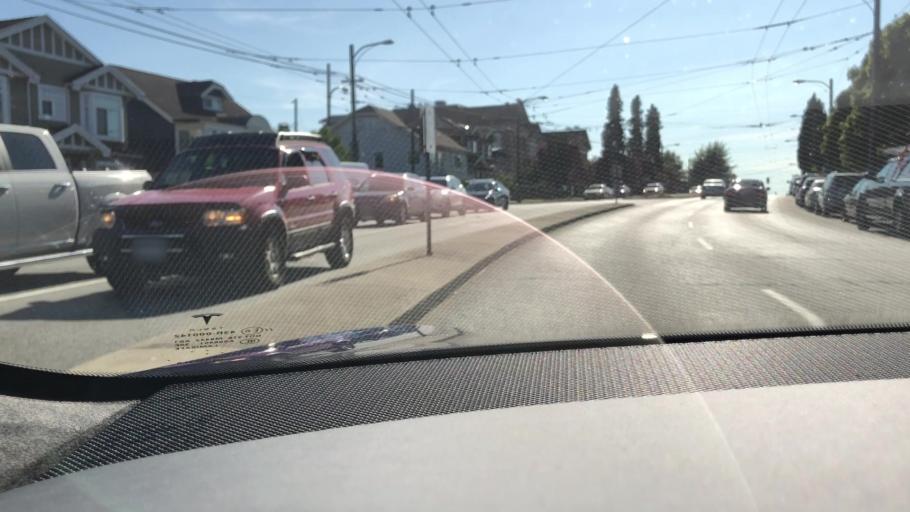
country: CA
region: British Columbia
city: Vancouver
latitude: 49.2327
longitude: -123.0661
